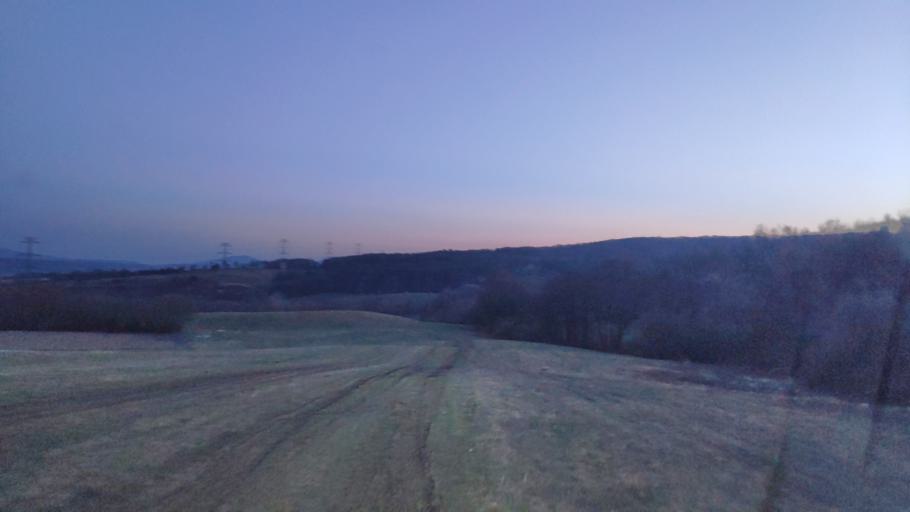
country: SK
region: Kosicky
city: Kosice
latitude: 48.8259
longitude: 21.2643
